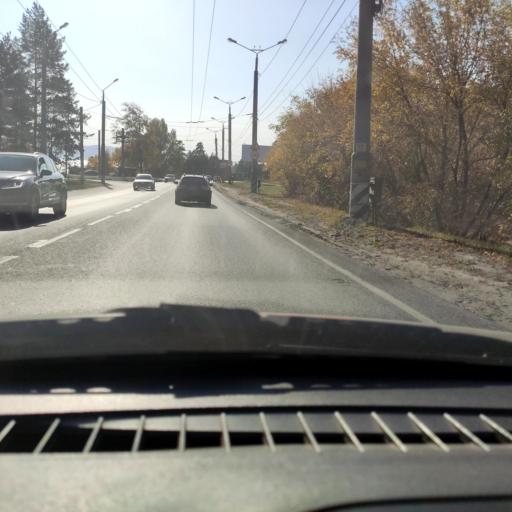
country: RU
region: Samara
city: Tol'yatti
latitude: 53.4771
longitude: 49.3494
